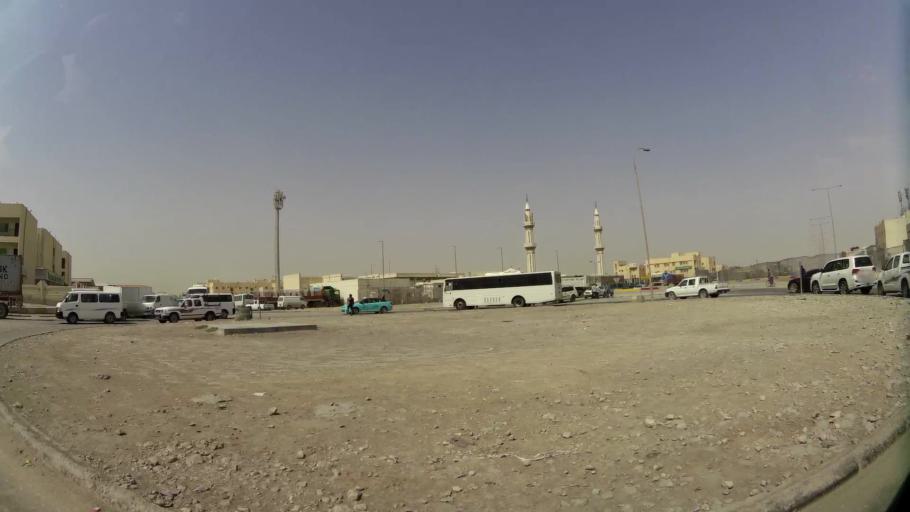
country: QA
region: Baladiyat ar Rayyan
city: Ar Rayyan
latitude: 25.1942
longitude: 51.4327
